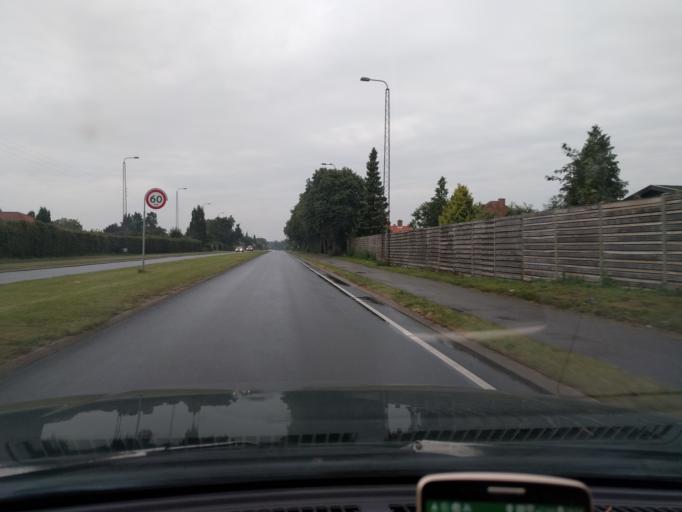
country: DK
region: Zealand
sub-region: Naestved Kommune
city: Naestved
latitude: 55.2111
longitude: 11.7538
